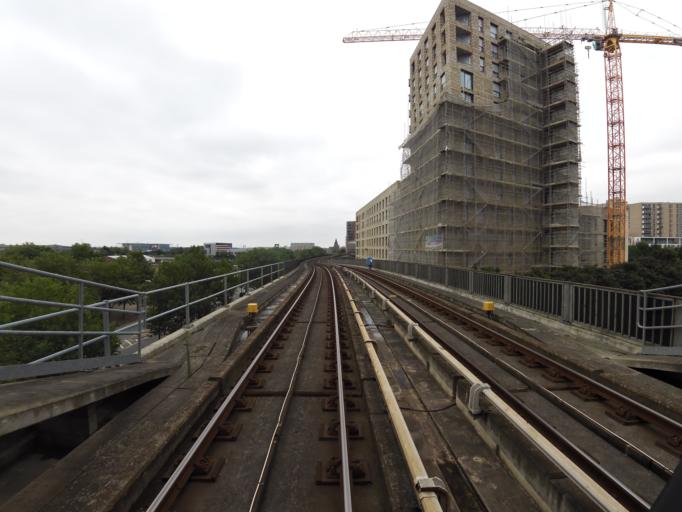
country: GB
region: England
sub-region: Greater London
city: Woolwich
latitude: 51.5023
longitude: 0.0334
